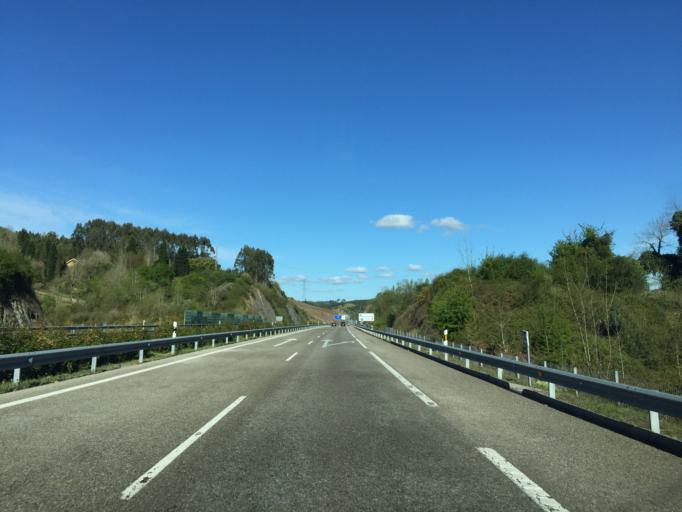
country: ES
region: Asturias
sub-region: Province of Asturias
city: Castandiello
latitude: 43.3570
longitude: -5.9408
